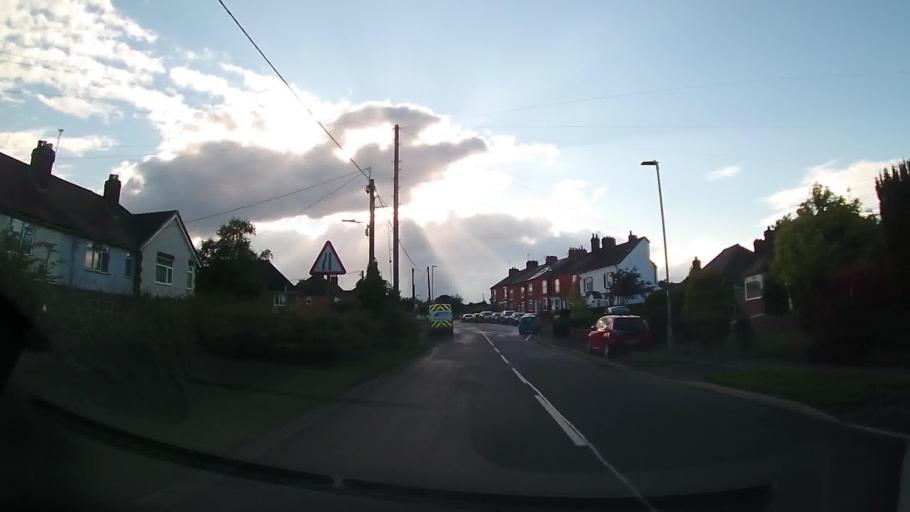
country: GB
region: England
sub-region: Leicestershire
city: Markfield
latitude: 52.6827
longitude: -1.2783
